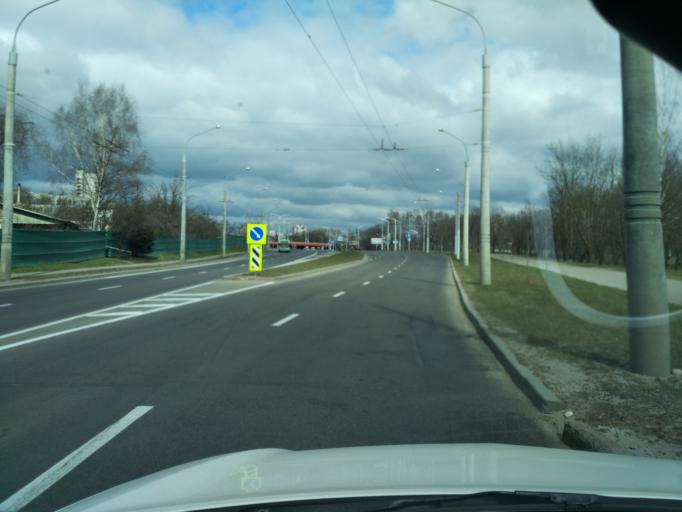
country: BY
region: Minsk
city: Novoye Medvezhino
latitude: 53.8673
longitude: 27.4954
